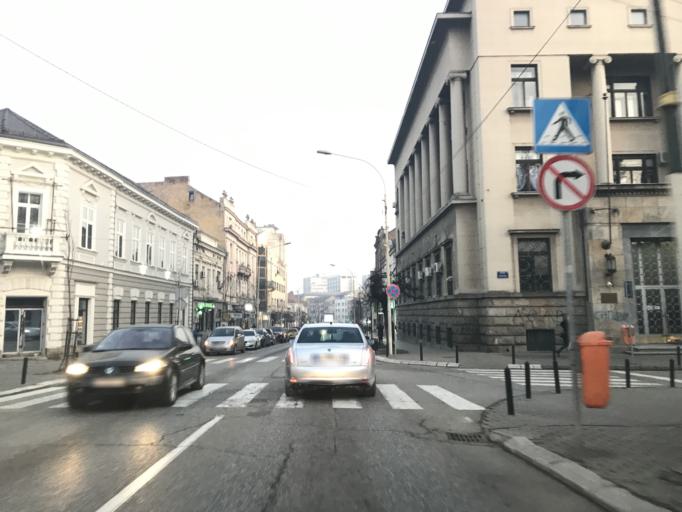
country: RS
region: Central Serbia
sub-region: Sumadijski Okrug
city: Kragujevac
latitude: 44.0121
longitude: 20.9127
